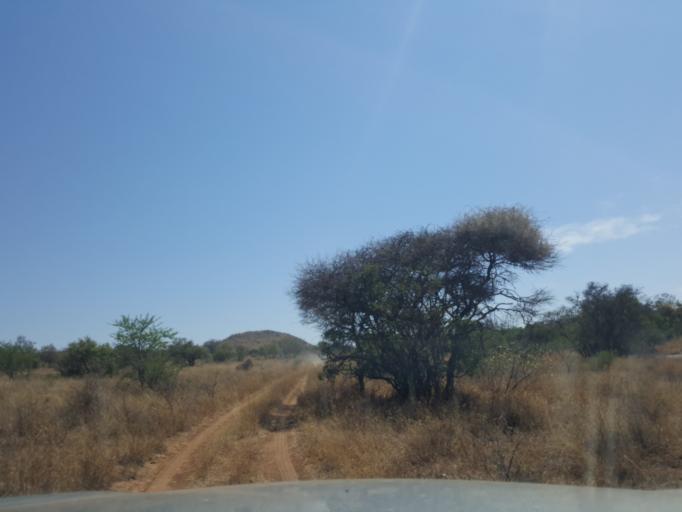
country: BW
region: South East
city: Lobatse
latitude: -25.1396
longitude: 25.6713
